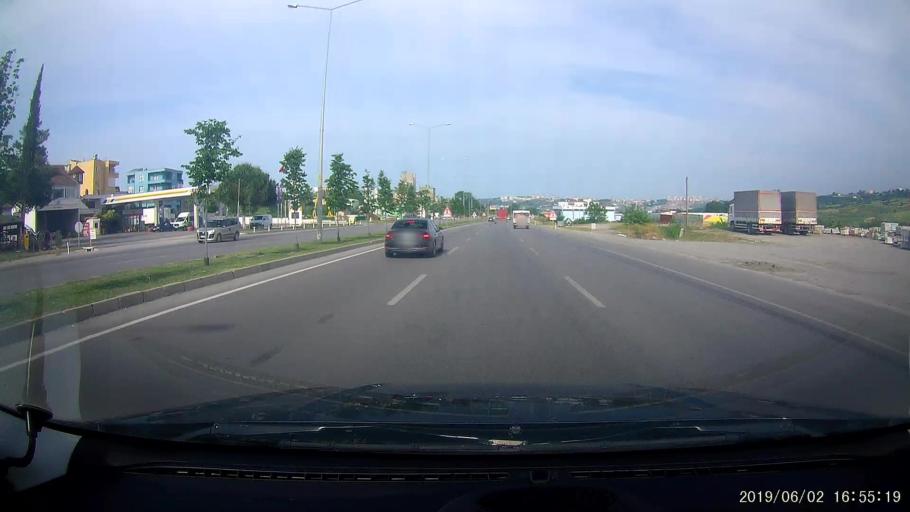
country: TR
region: Samsun
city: Samsun
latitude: 41.2928
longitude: 36.2517
